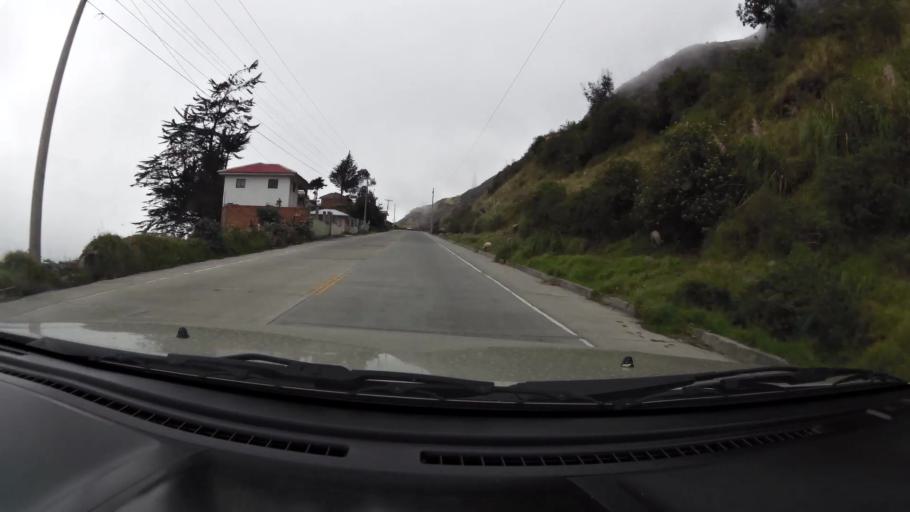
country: EC
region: Canar
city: Canar
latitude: -2.4844
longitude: -78.9931
